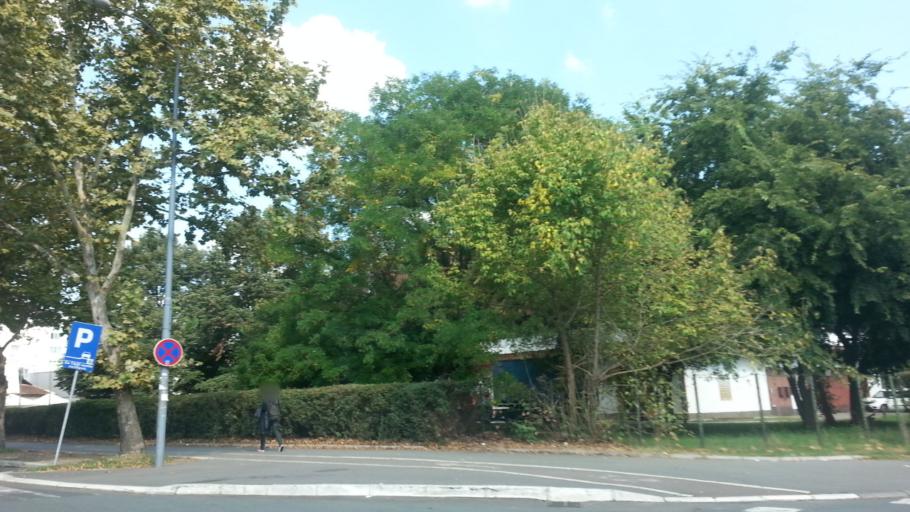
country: RS
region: Central Serbia
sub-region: Belgrade
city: Novi Beograd
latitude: 44.8022
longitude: 20.3886
